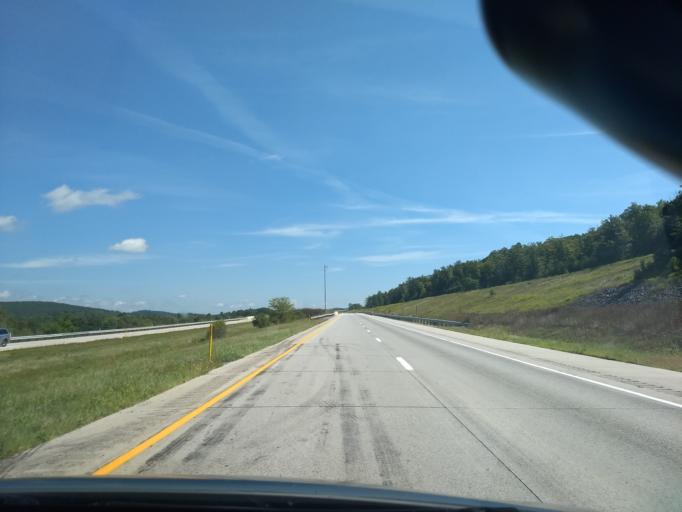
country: US
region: Pennsylvania
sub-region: Blair County
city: Tyrone
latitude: 40.7100
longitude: -78.1905
